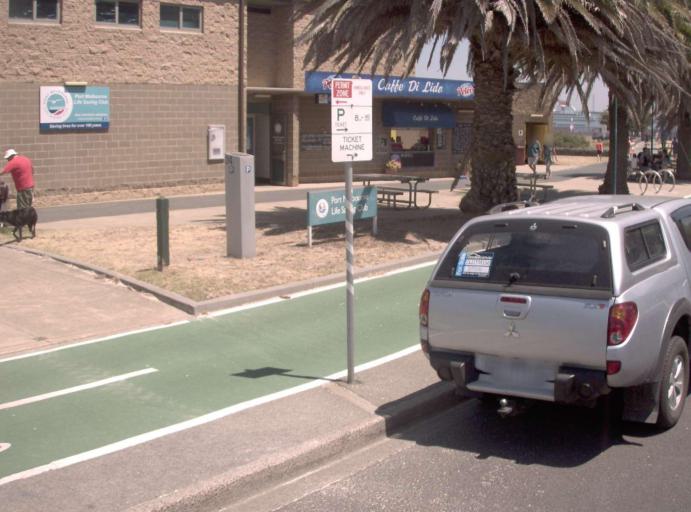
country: AU
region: Victoria
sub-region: Port Phillip
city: Port Melbourne
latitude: -37.8449
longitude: 144.9425
